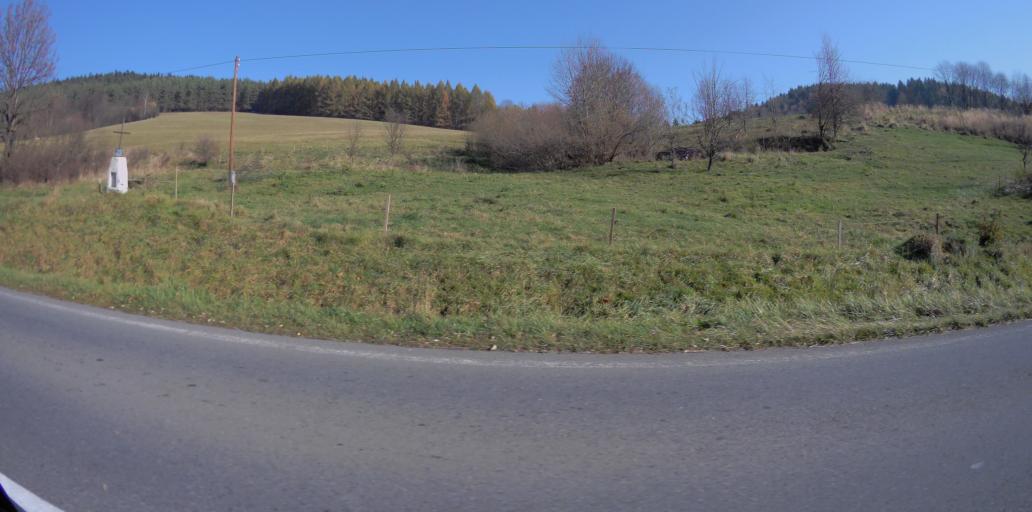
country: PL
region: Subcarpathian Voivodeship
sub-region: Powiat bieszczadzki
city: Ustrzyki Dolne
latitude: 49.4862
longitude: 22.6607
